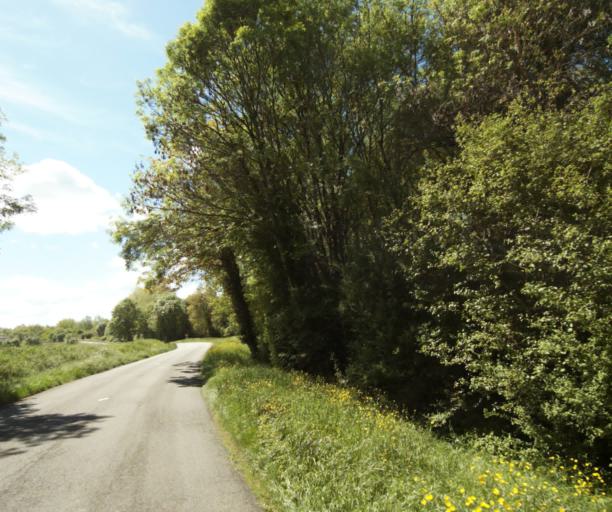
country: FR
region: Poitou-Charentes
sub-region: Departement de la Charente-Maritime
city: Chaniers
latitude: 45.7295
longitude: -0.5103
